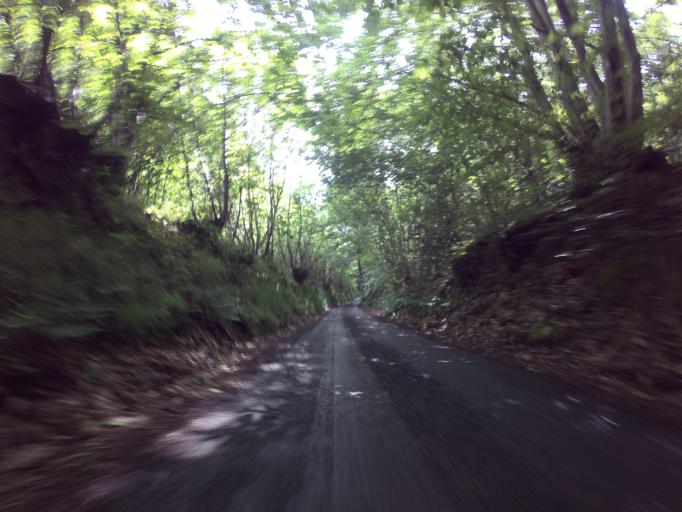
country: GB
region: England
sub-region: Kent
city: Halstead
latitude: 51.3437
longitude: 0.1500
